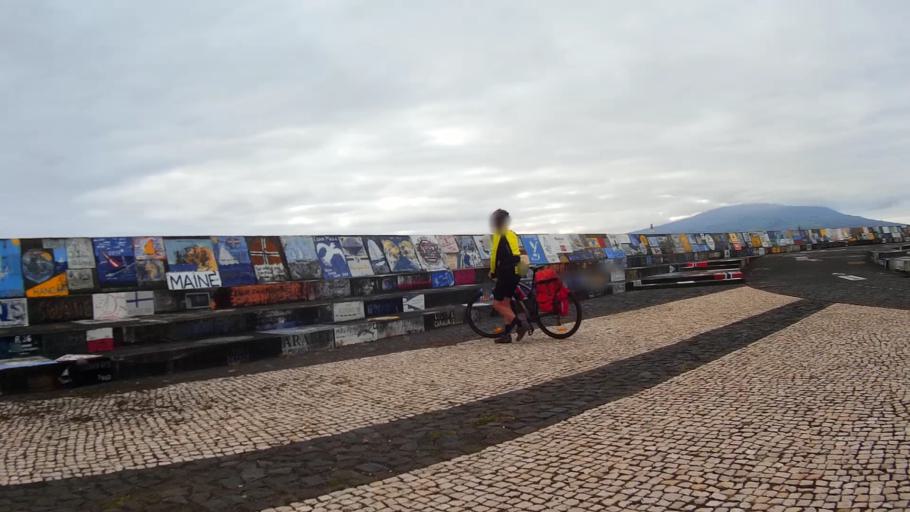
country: PT
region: Azores
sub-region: Horta
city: Horta
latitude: 38.5346
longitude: -28.6257
